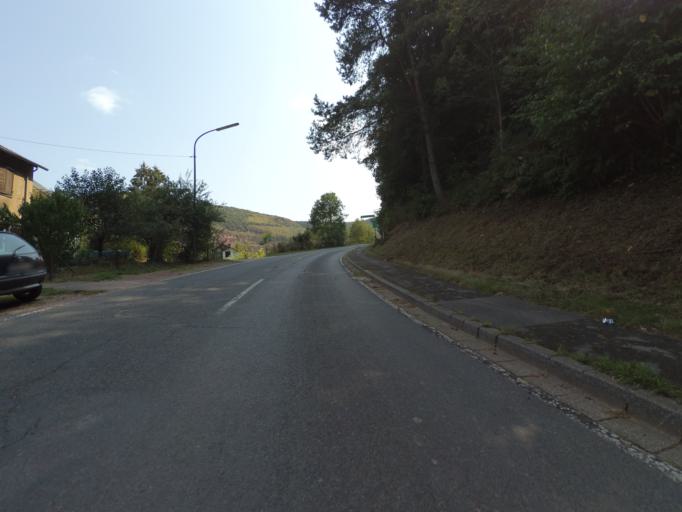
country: DE
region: Rheinland-Pfalz
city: Taben-Rodt
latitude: 49.5509
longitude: 6.5998
